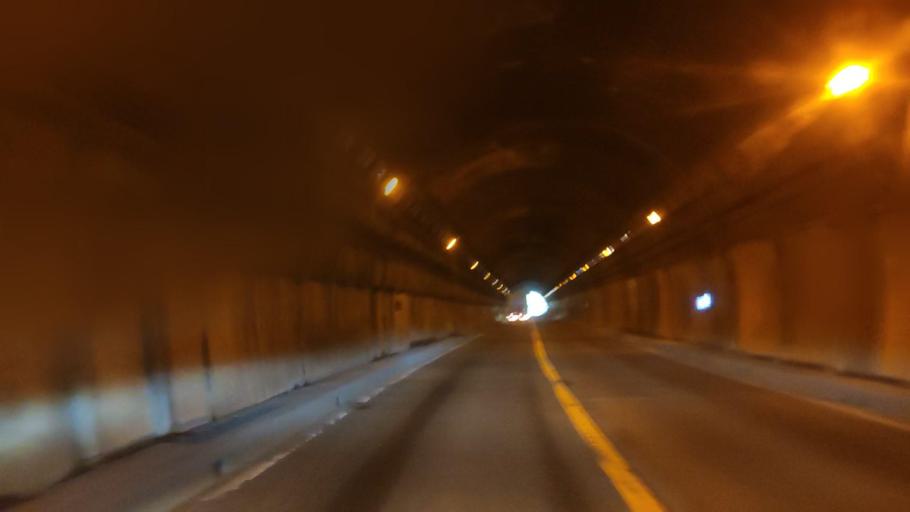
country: JP
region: Shizuoka
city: Fujinomiya
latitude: 35.2072
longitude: 138.5159
